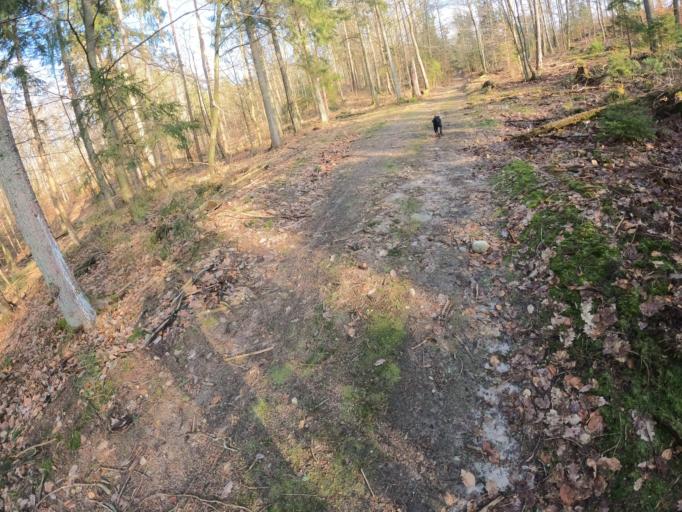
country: PL
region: West Pomeranian Voivodeship
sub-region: Powiat koszalinski
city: Polanow
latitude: 54.1270
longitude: 16.7144
